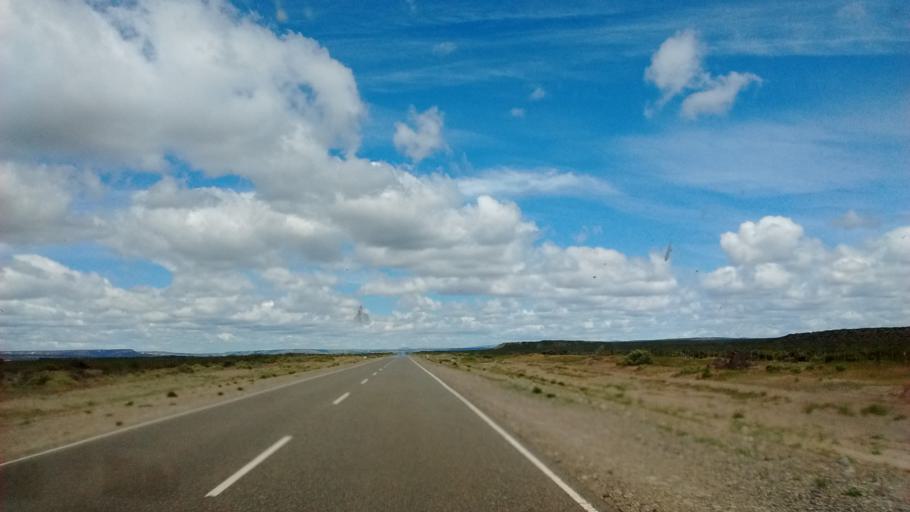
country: AR
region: Neuquen
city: Piedra del Aguila
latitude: -39.8363
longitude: -69.7679
